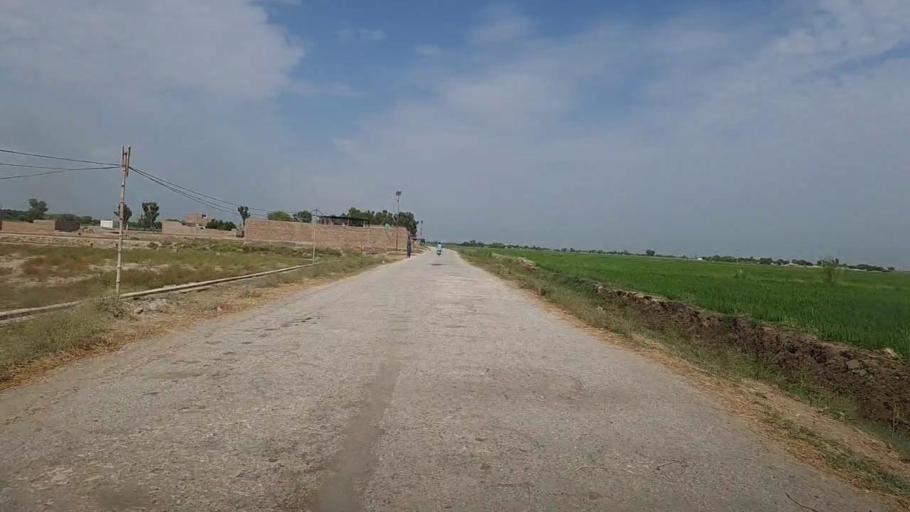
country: PK
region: Sindh
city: Thul
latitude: 28.2309
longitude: 68.7941
